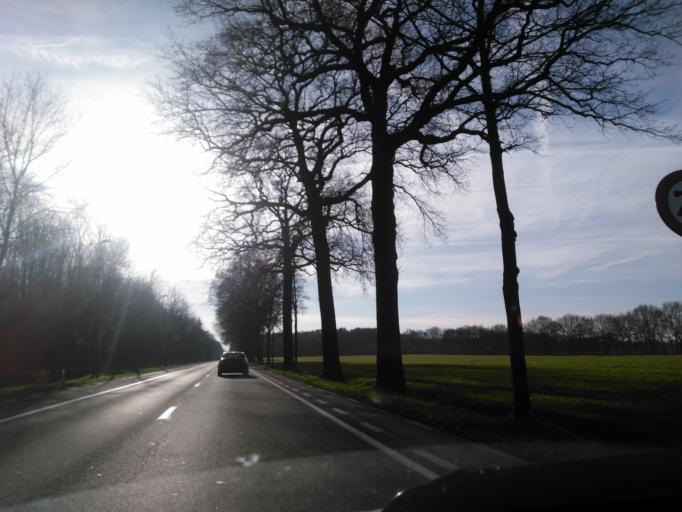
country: NL
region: Zeeland
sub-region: Gemeente Hulst
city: Hulst
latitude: 51.2441
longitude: 4.0630
